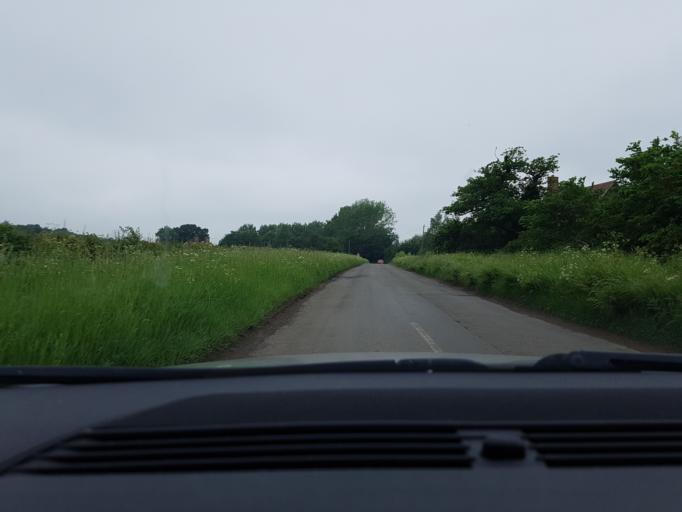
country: GB
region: England
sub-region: Buckinghamshire
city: Winslow
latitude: 51.9445
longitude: -0.9057
